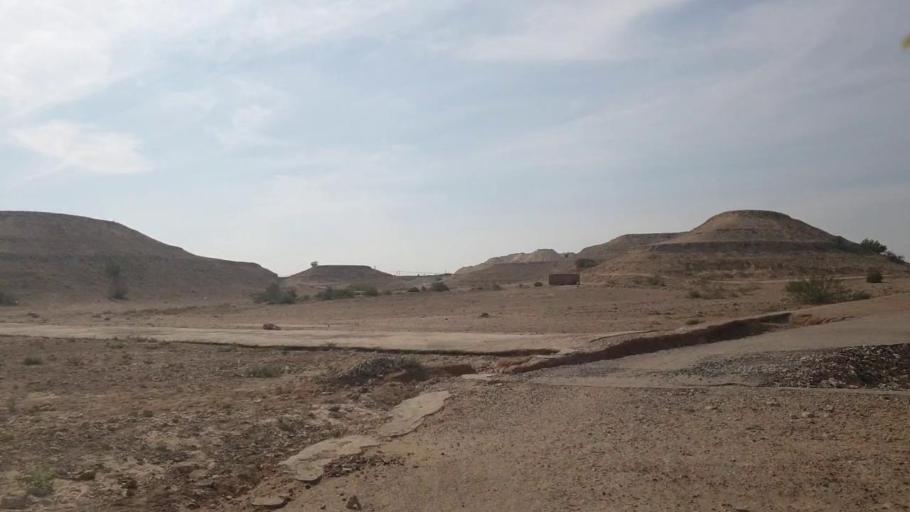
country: PK
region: Sindh
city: Hala
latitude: 25.7389
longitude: 68.2935
